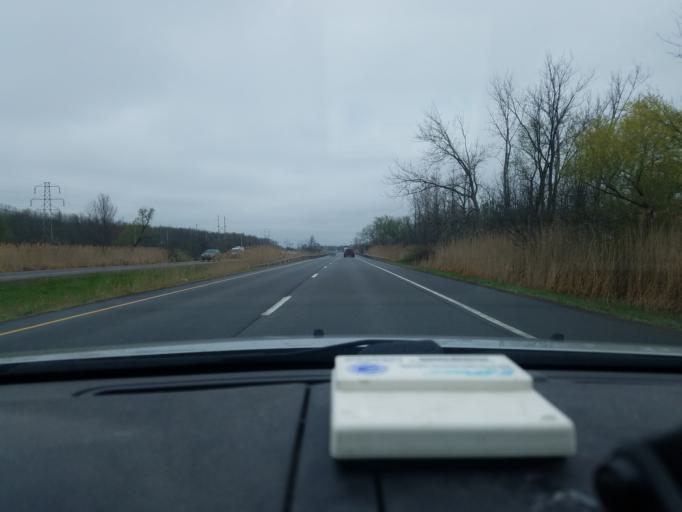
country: US
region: New York
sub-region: Onondaga County
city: East Syracuse
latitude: 43.1136
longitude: -76.0776
